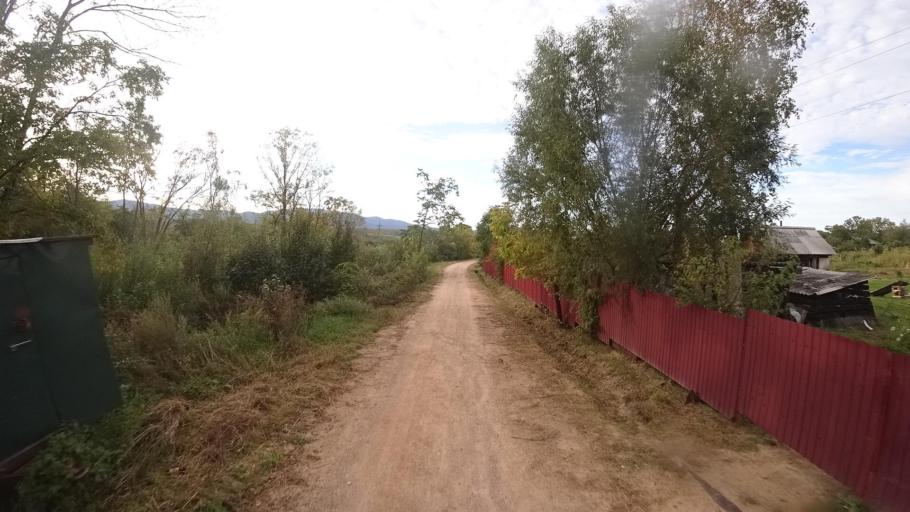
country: RU
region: Primorskiy
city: Yakovlevka
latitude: 44.4115
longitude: 133.4517
